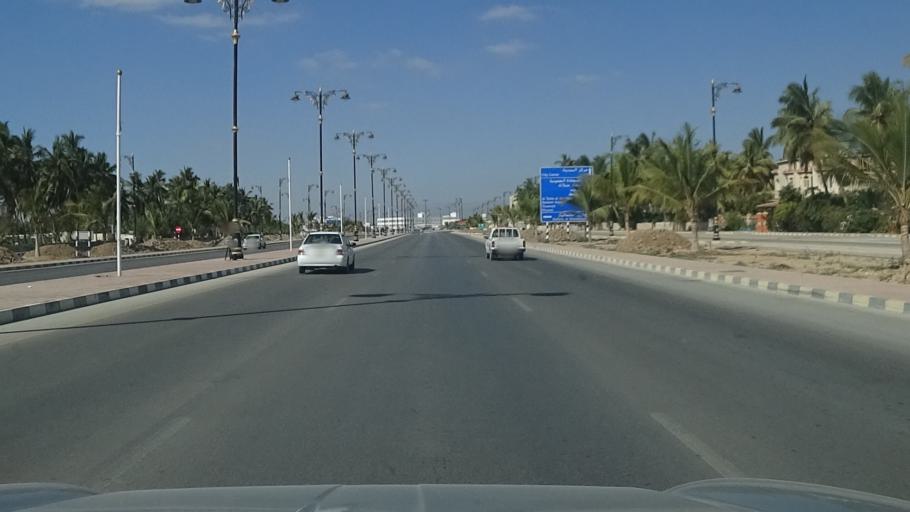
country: OM
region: Zufar
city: Salalah
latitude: 17.0365
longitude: 54.1533
